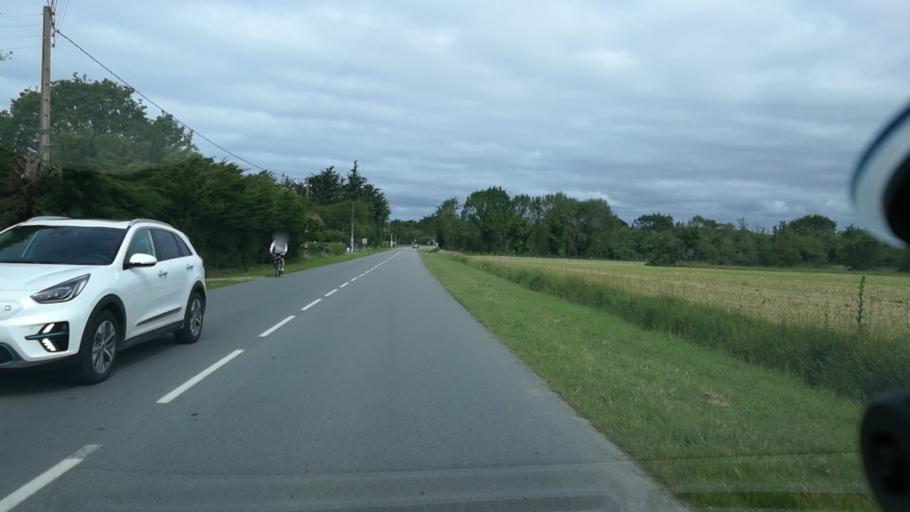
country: FR
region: Brittany
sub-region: Departement du Morbihan
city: Penestin
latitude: 47.4576
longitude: -2.4740
